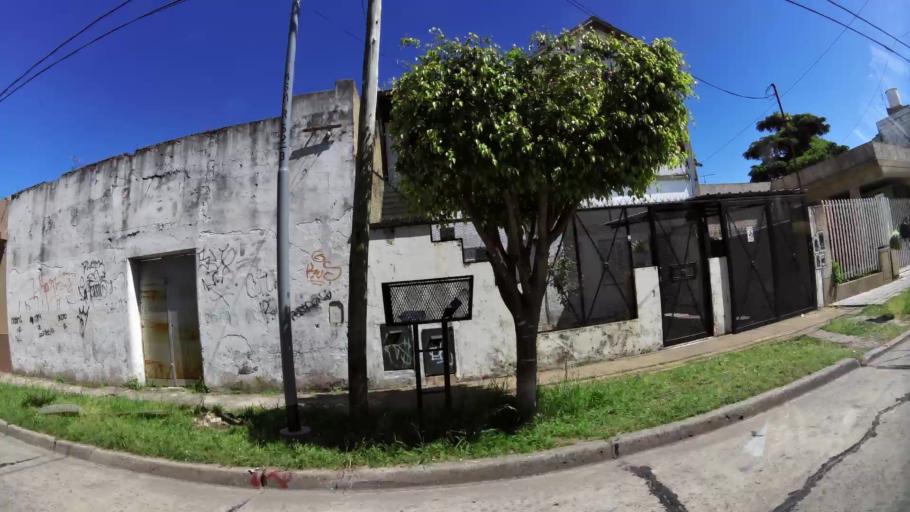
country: AR
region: Buenos Aires
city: Caseros
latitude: -34.5906
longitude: -58.5454
